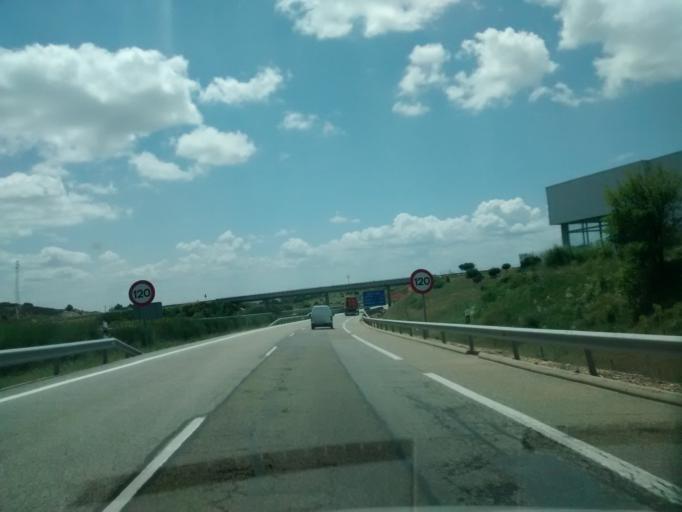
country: ES
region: Castille and Leon
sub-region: Provincia de Leon
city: Astorga
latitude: 42.4691
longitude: -6.0826
